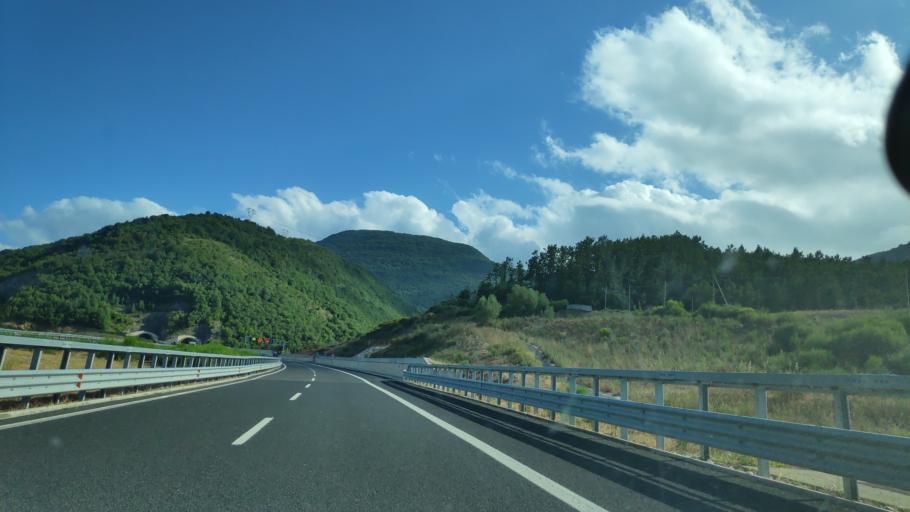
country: IT
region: Campania
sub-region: Provincia di Salerno
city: Casalbuono
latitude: 40.2187
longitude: 15.6717
